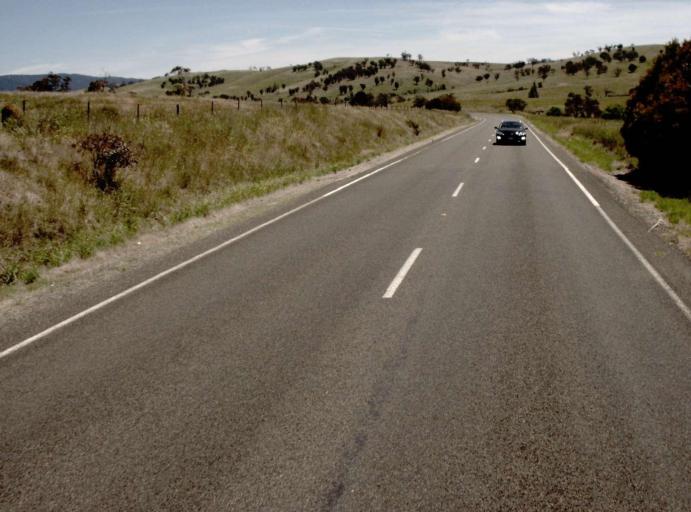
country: AU
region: Victoria
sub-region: Alpine
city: Mount Beauty
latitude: -37.1356
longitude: 147.6457
